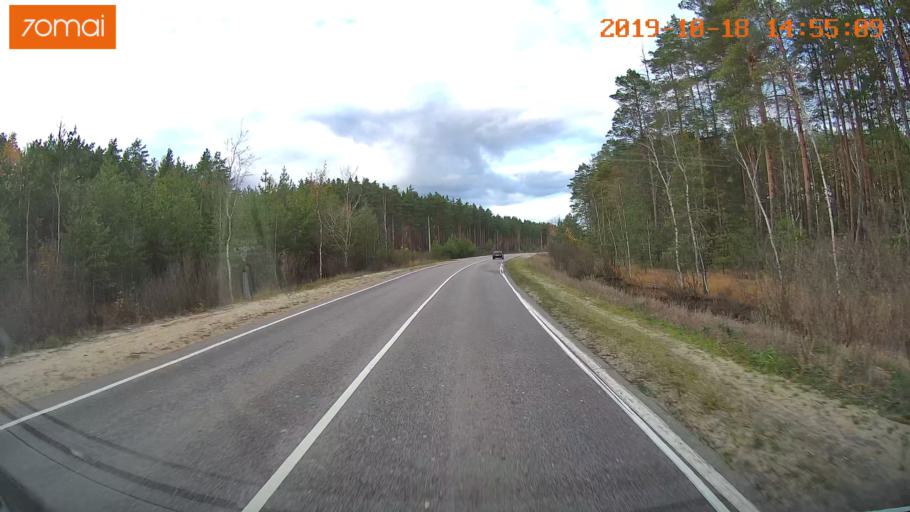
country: RU
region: Vladimir
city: Kurlovo
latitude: 55.4480
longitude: 40.5889
